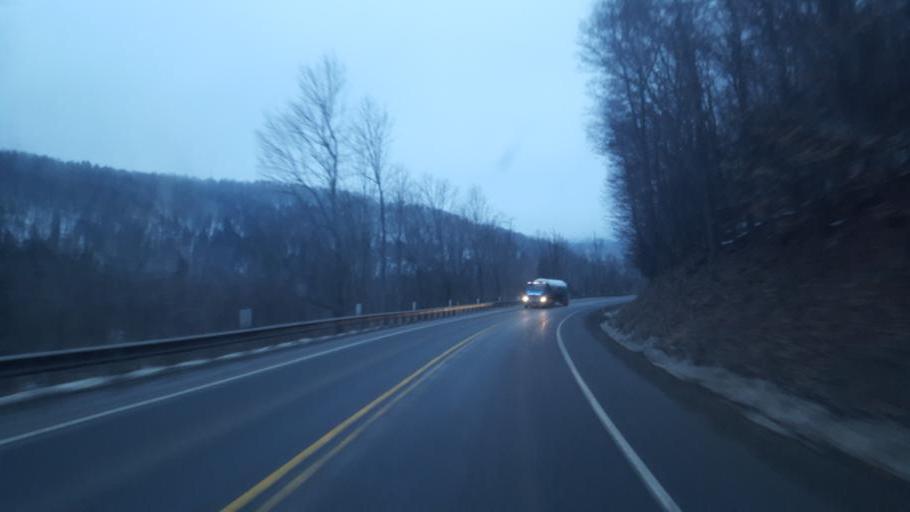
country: US
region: Pennsylvania
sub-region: Potter County
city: Coudersport
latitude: 41.7427
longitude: -78.0781
